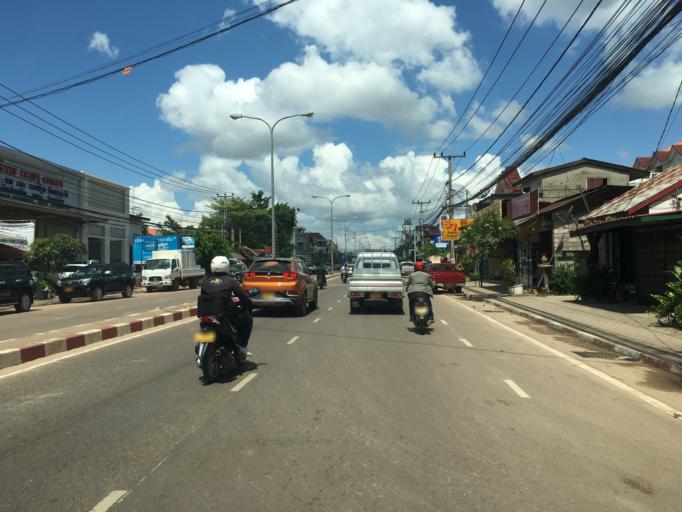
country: TH
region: Nong Khai
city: Si Chiang Mai
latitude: 17.9736
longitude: 102.5615
